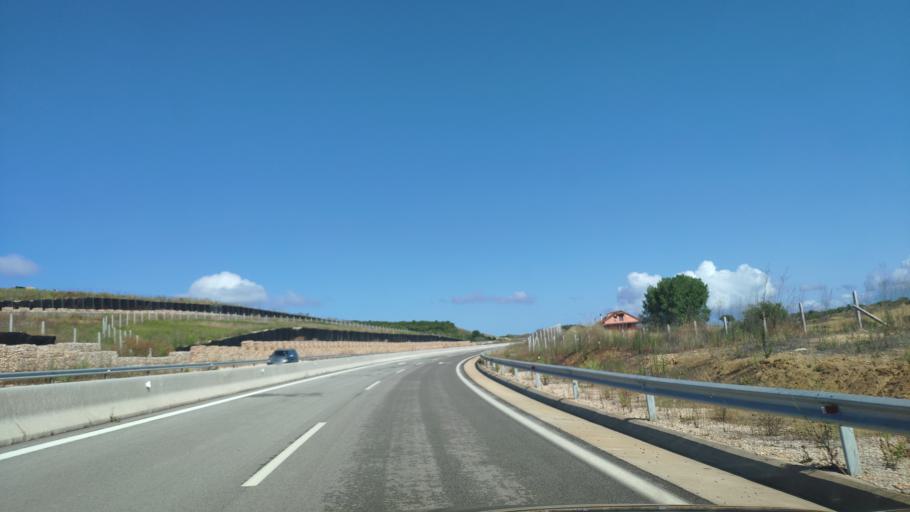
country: GR
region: West Greece
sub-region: Nomos Aitolias kai Akarnanias
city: Vonitsa
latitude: 38.9106
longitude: 20.8321
